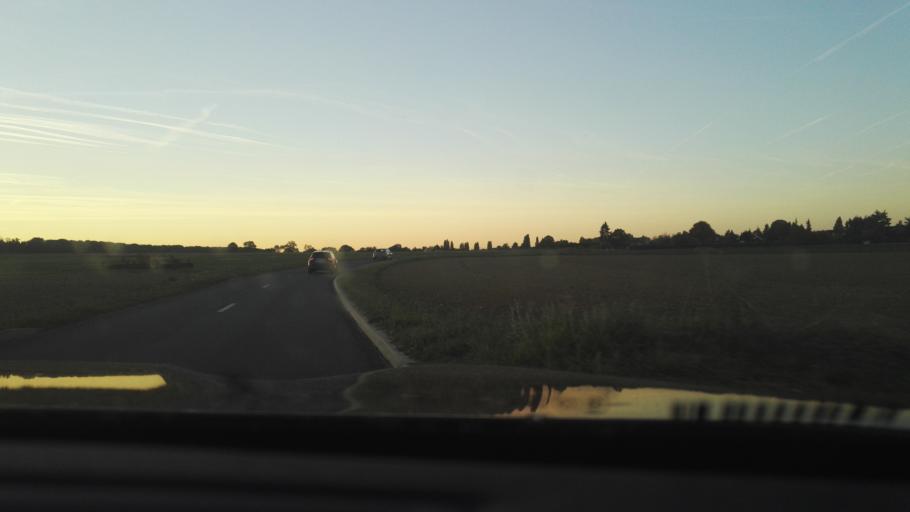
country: FR
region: Ile-de-France
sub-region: Departement des Yvelines
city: Houdan
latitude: 48.8534
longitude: 1.5917
